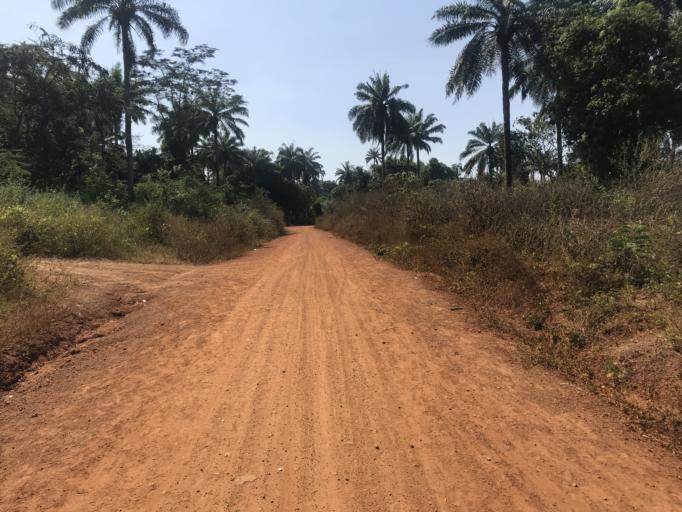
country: NG
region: Osun
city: Ikirun
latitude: 7.9341
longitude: 4.6355
